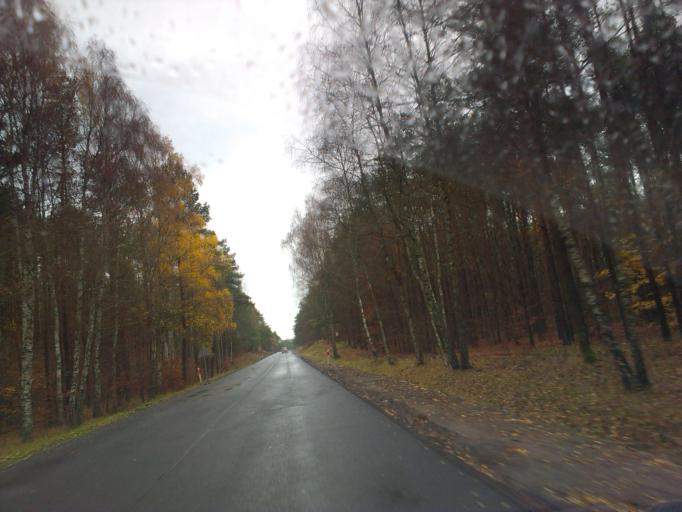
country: PL
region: West Pomeranian Voivodeship
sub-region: Powiat szczecinecki
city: Lubowo
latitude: 53.5977
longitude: 16.4290
